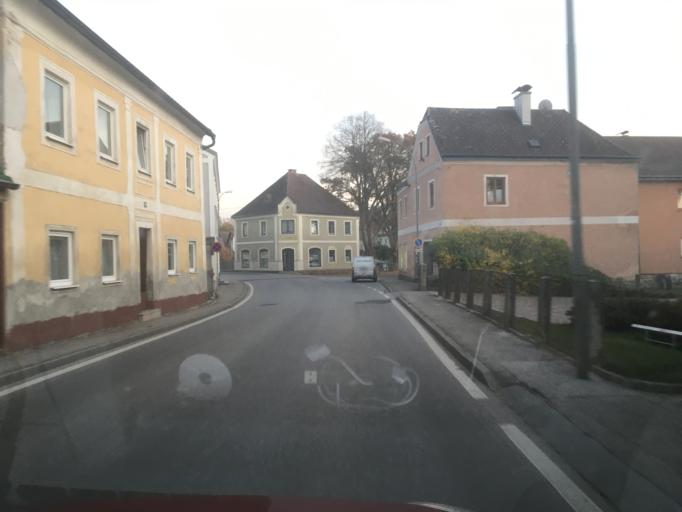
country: AT
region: Lower Austria
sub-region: Politischer Bezirk Zwettl
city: Gross-Gerungs
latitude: 48.5732
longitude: 14.9617
